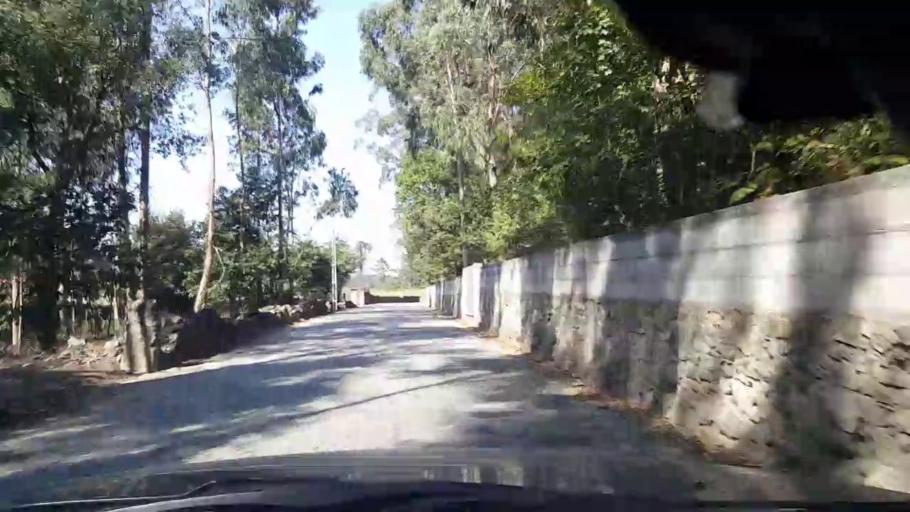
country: PT
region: Porto
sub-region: Povoa de Varzim
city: Pedroso
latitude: 41.4066
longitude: -8.7074
